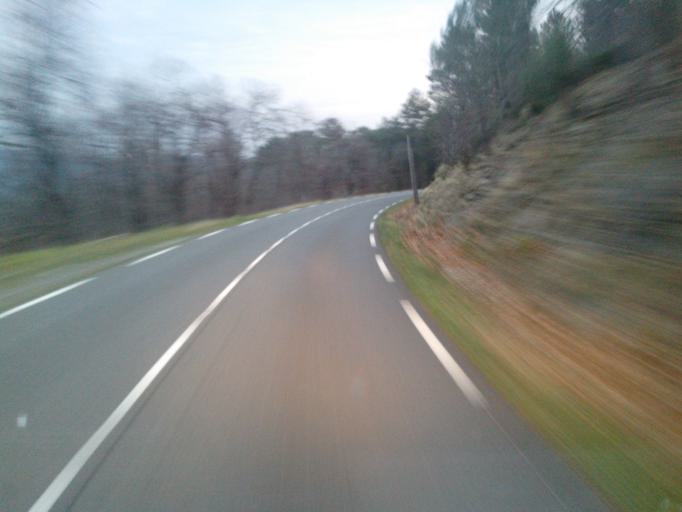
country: FR
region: Languedoc-Roussillon
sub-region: Departement du Gard
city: Saint-Jean-du-Gard
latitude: 44.1522
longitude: 3.7607
